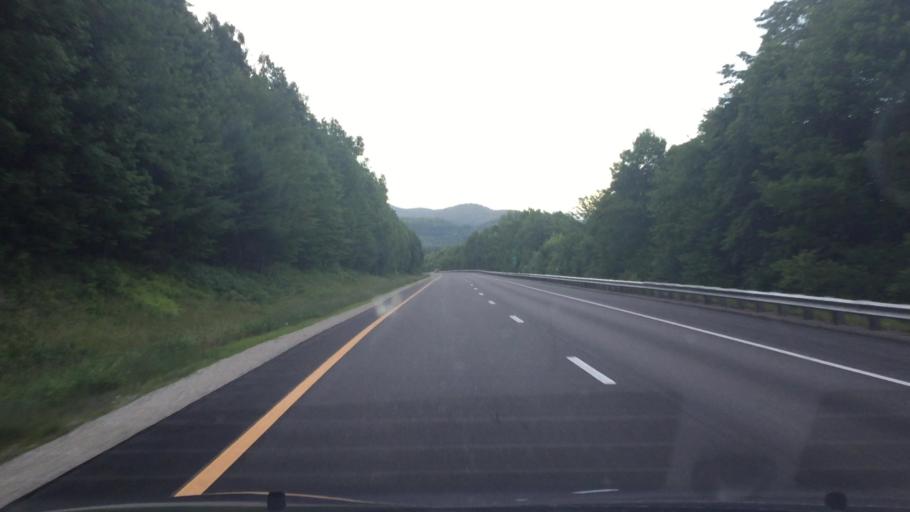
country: US
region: New Hampshire
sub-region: Grafton County
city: Thornton
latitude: 43.9004
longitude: -71.6882
